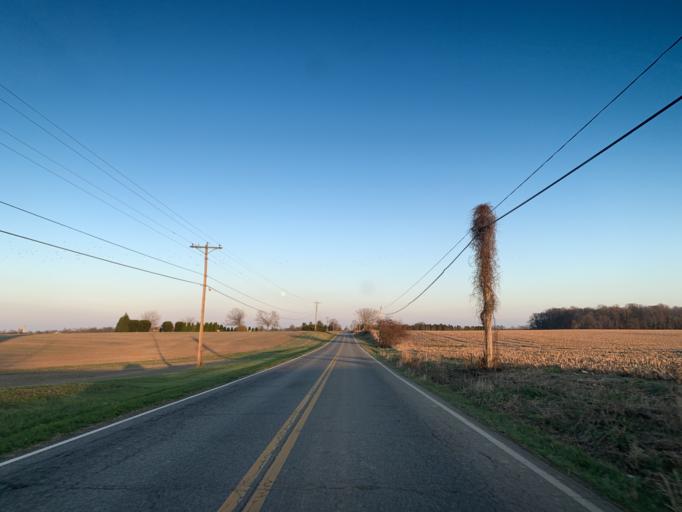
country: US
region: Maryland
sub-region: Cecil County
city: Charlestown
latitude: 39.4084
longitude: -75.9323
